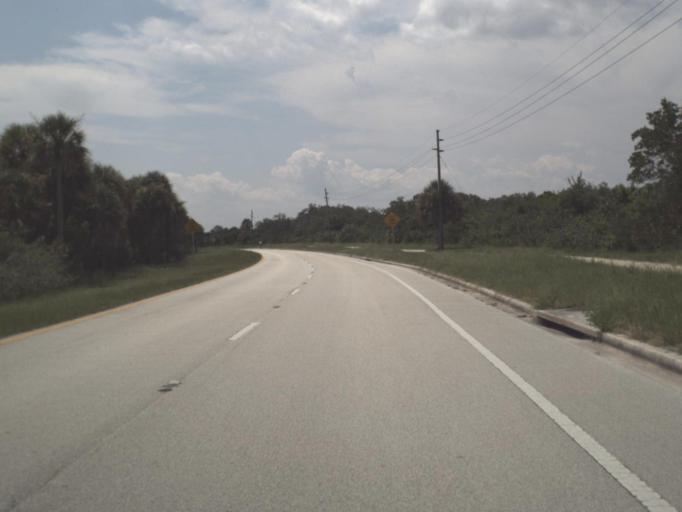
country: US
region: Florida
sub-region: Pinellas County
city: Tierra Verde
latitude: 27.6627
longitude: -82.7247
